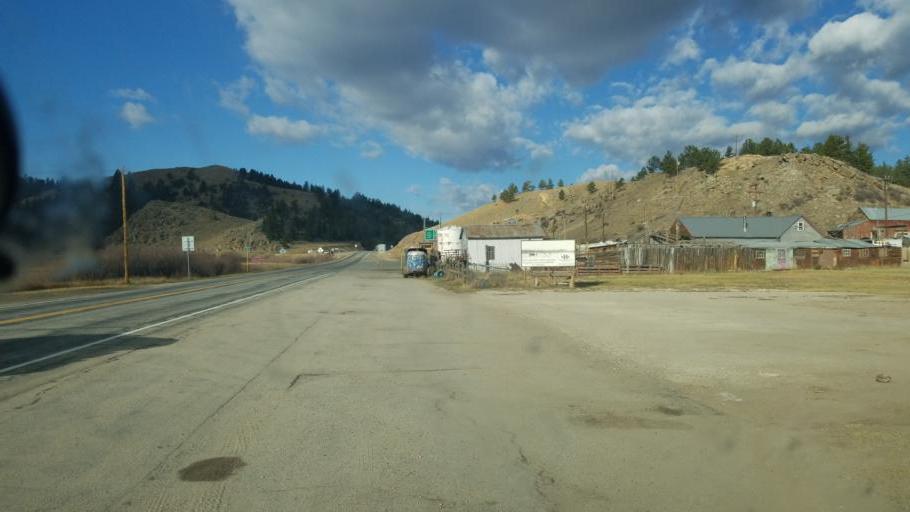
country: US
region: Colorado
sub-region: Park County
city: Fairplay
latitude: 39.0212
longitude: -105.7966
